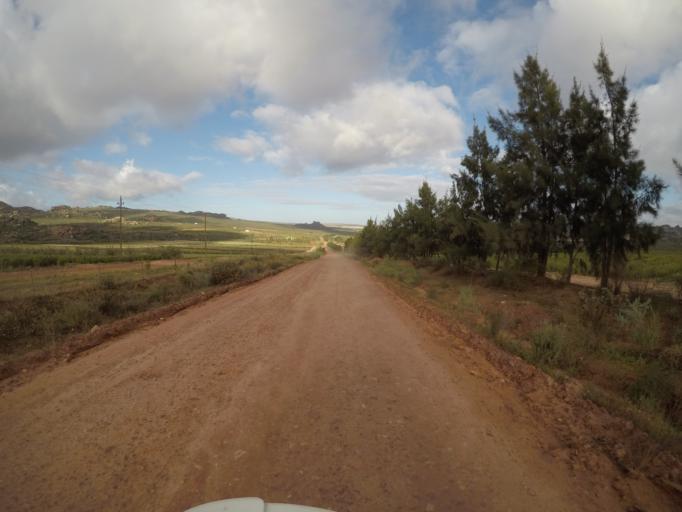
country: ZA
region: Western Cape
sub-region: West Coast District Municipality
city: Clanwilliam
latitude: -32.3447
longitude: 18.7536
